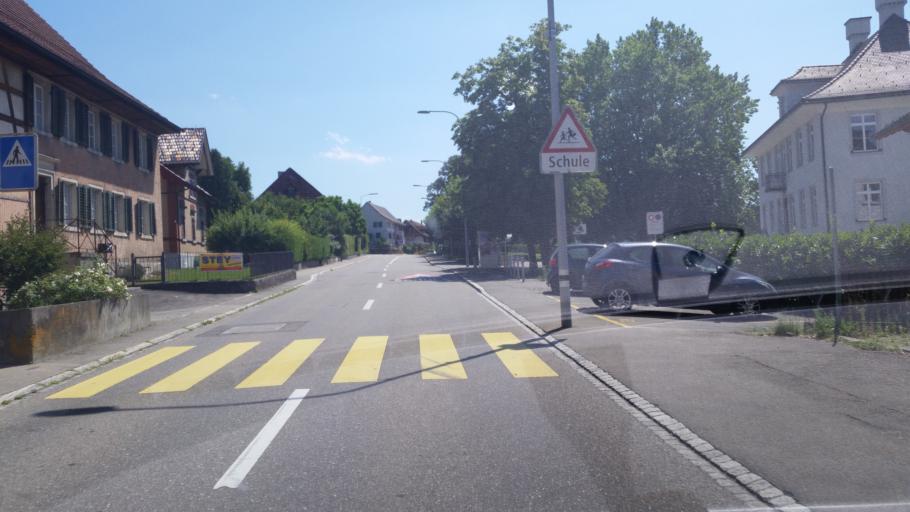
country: CH
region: Zurich
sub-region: Bezirk Buelach
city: Glattfelden
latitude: 47.5594
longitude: 8.5010
